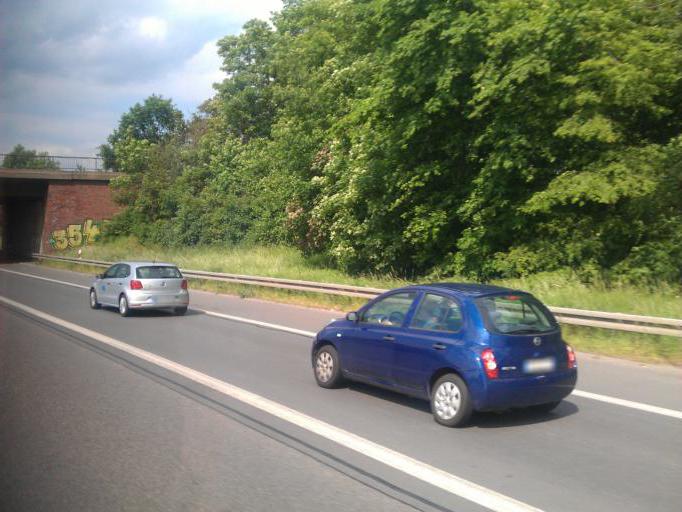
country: DE
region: North Rhine-Westphalia
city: Wesseling
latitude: 50.8469
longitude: 6.9680
